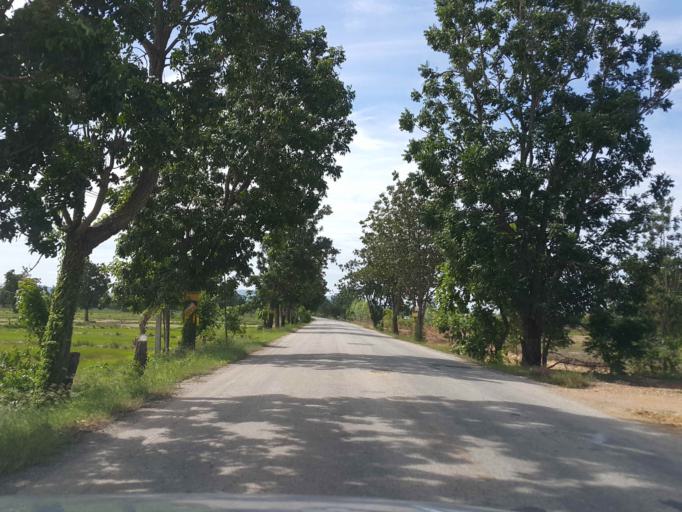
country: TH
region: Sukhothai
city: Ban Dan Lan Hoi
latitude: 17.1317
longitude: 99.5277
